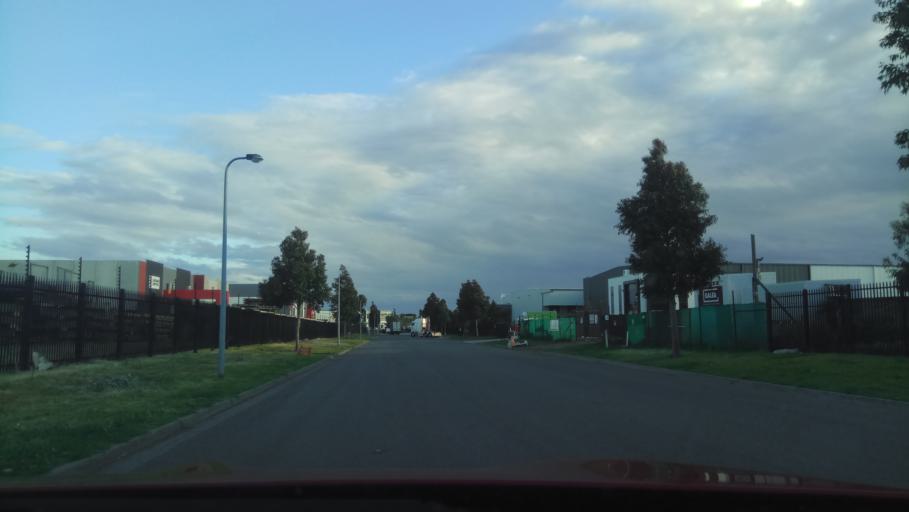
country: AU
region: Victoria
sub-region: Hobsons Bay
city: Altona
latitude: -37.8527
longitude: 144.8255
